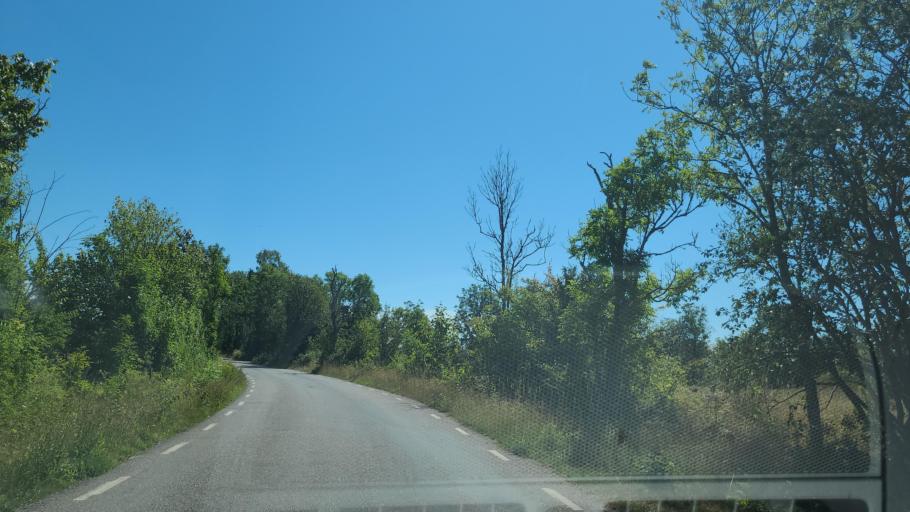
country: SE
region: Kalmar
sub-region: Borgholms Kommun
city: Borgholm
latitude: 56.7444
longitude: 16.6998
